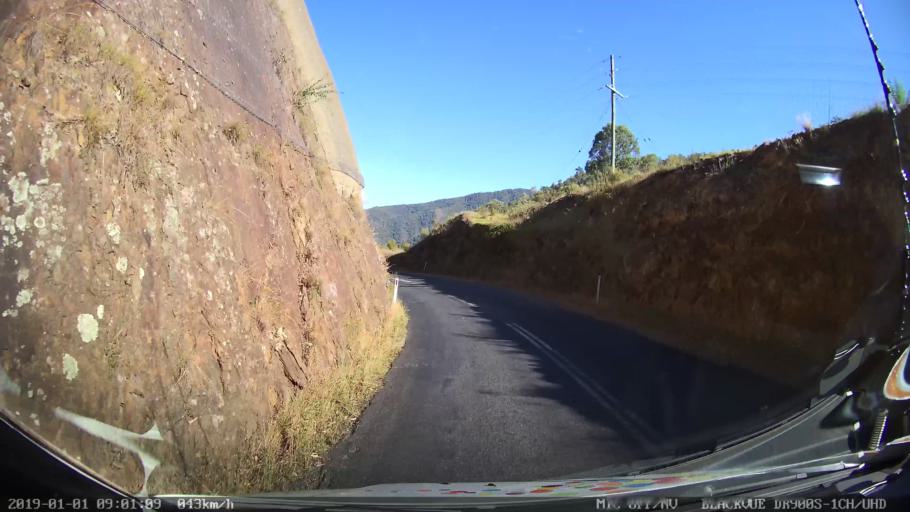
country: AU
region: New South Wales
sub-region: Snowy River
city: Jindabyne
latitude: -36.2344
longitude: 148.1776
